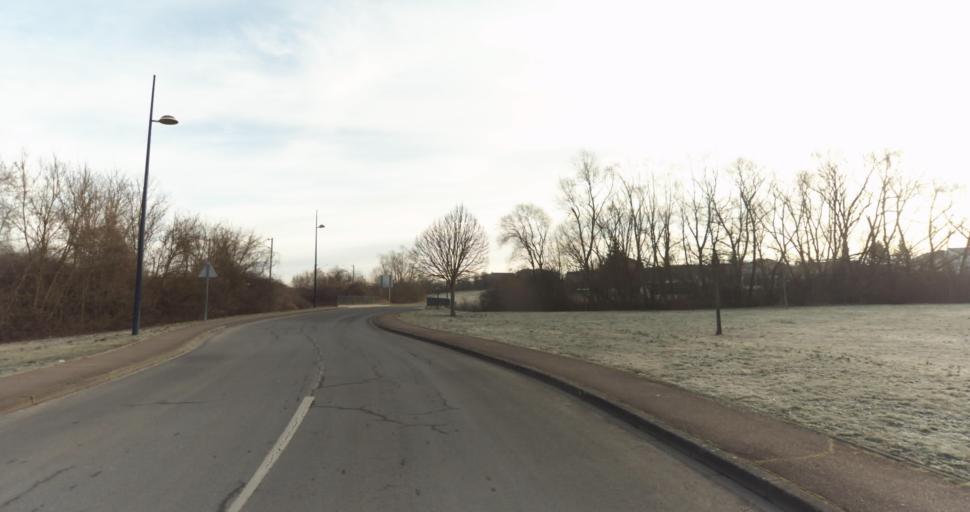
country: FR
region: Lorraine
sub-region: Departement de Meurthe-et-Moselle
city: Labry
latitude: 49.1661
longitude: 5.8826
